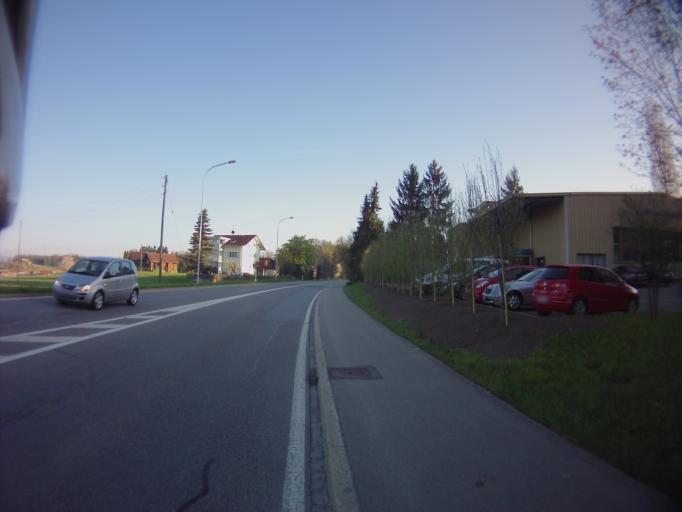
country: CH
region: Zug
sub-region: Zug
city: Cham
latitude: 47.1971
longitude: 8.4529
